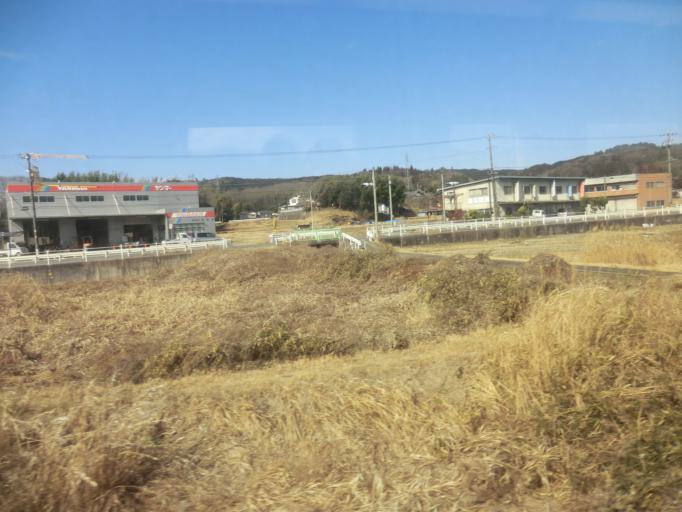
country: JP
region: Gifu
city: Mizunami
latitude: 35.3727
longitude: 137.2605
